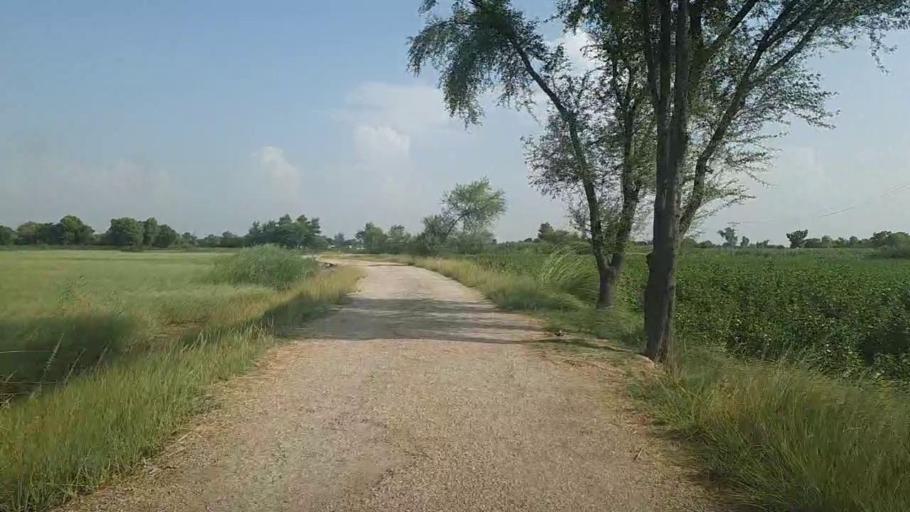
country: PK
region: Sindh
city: Ubauro
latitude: 28.1708
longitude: 69.7737
